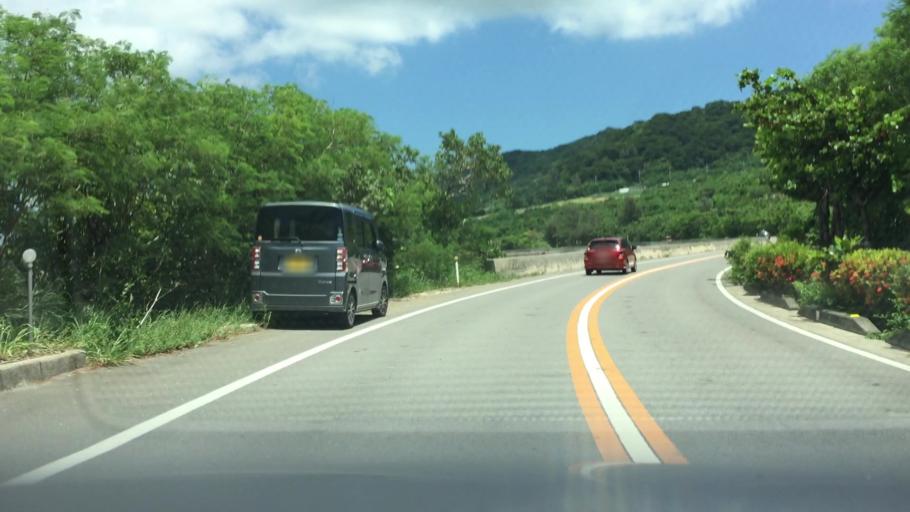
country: JP
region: Okinawa
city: Ishigaki
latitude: 24.4288
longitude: 124.1245
